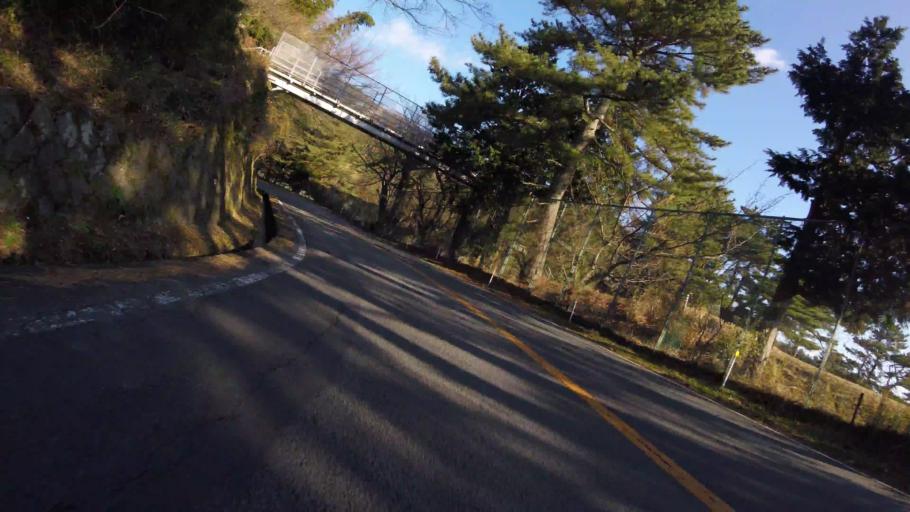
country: JP
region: Shizuoka
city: Atami
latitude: 35.1079
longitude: 139.0546
